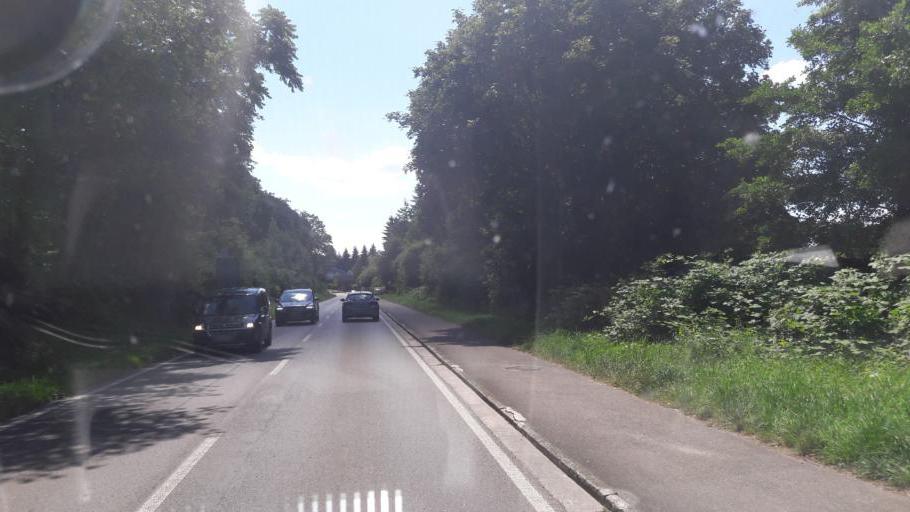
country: DE
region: Baden-Wuerttemberg
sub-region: Karlsruhe Region
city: Bruchsal
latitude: 49.1156
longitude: 8.5836
